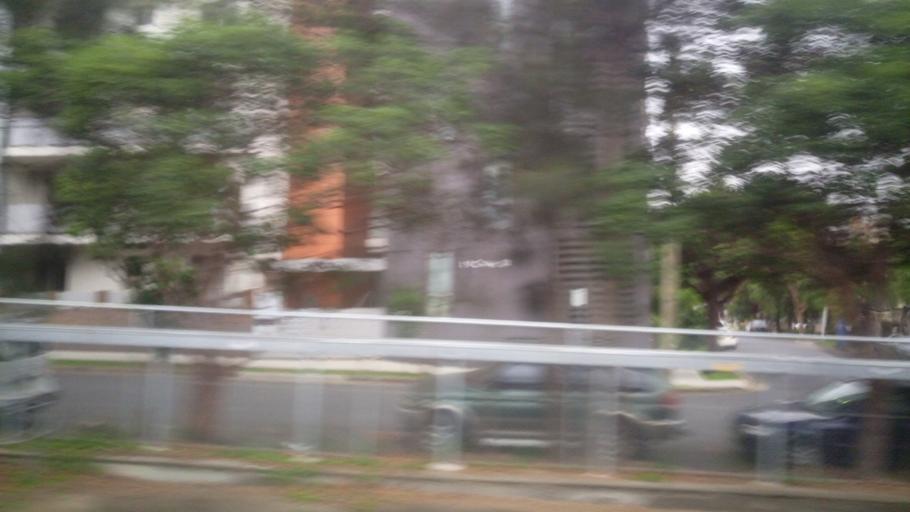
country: AU
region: New South Wales
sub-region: Strathfield
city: Homebush
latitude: -33.8647
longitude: 151.0799
